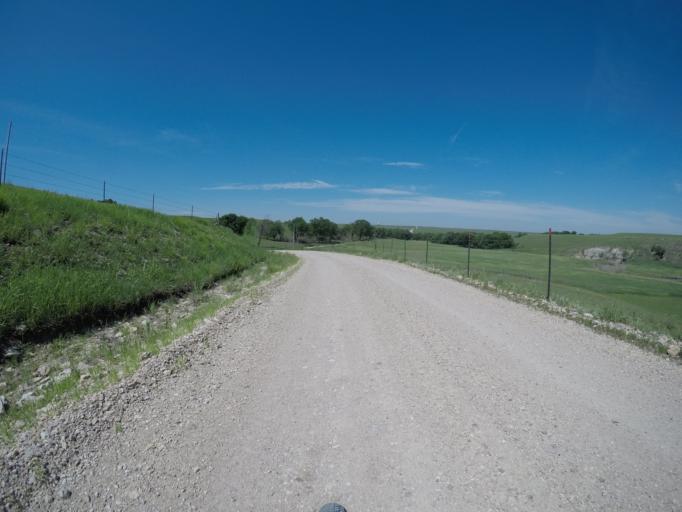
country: US
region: Kansas
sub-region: Wabaunsee County
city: Alma
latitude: 39.0011
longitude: -96.1962
